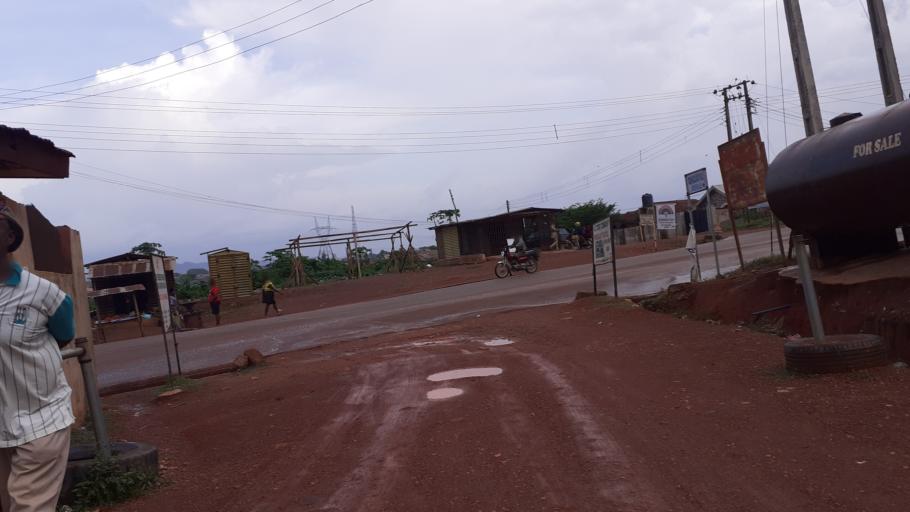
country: NG
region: Ondo
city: Akure
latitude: 7.2134
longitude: 5.2178
